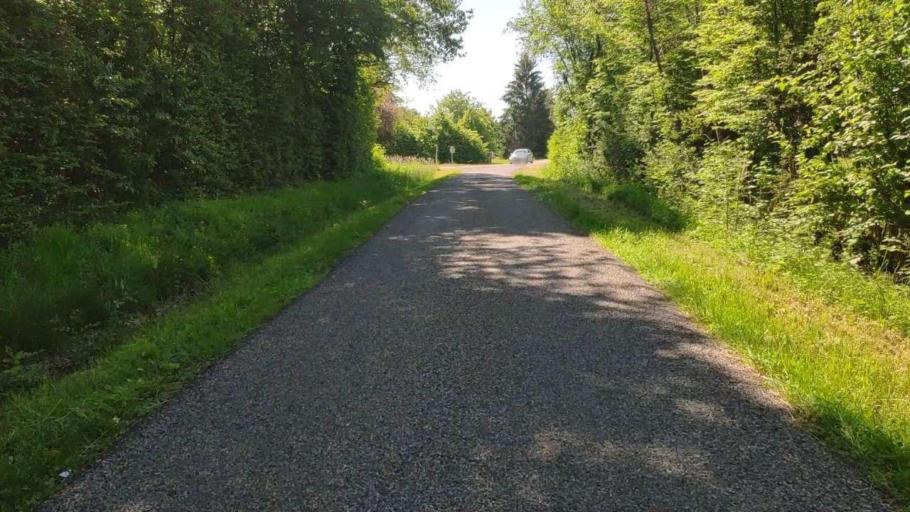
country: FR
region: Franche-Comte
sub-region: Departement du Jura
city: Bletterans
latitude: 46.8010
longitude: 5.4437
